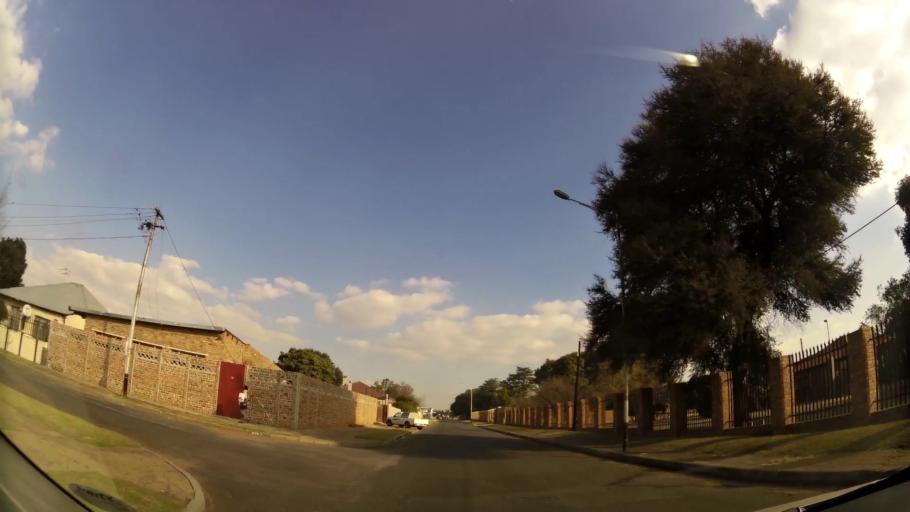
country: ZA
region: Gauteng
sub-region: West Rand District Municipality
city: Krugersdorp
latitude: -26.0958
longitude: 27.7434
